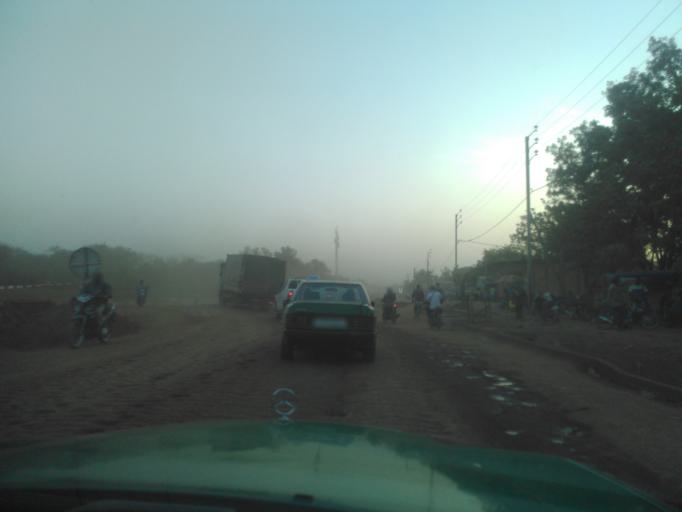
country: BF
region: Centre
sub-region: Kadiogo Province
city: Ouagadougou
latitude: 12.3839
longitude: -1.5042
